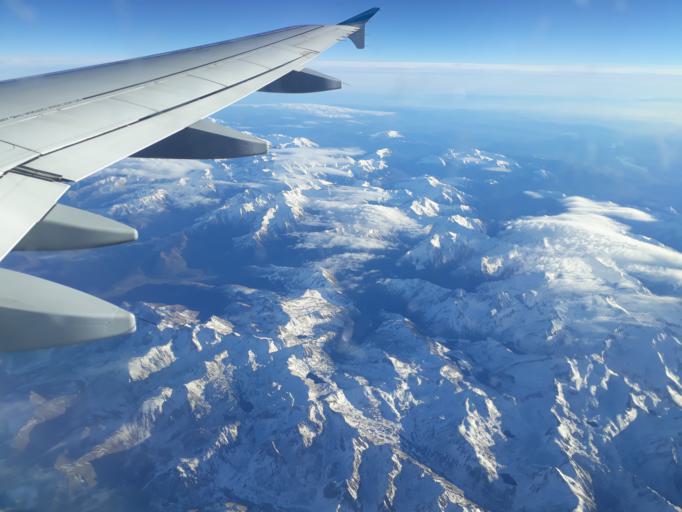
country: FR
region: Midi-Pyrenees
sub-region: Departement des Hautes-Pyrenees
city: Campan
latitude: 42.9713
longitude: 0.0860
